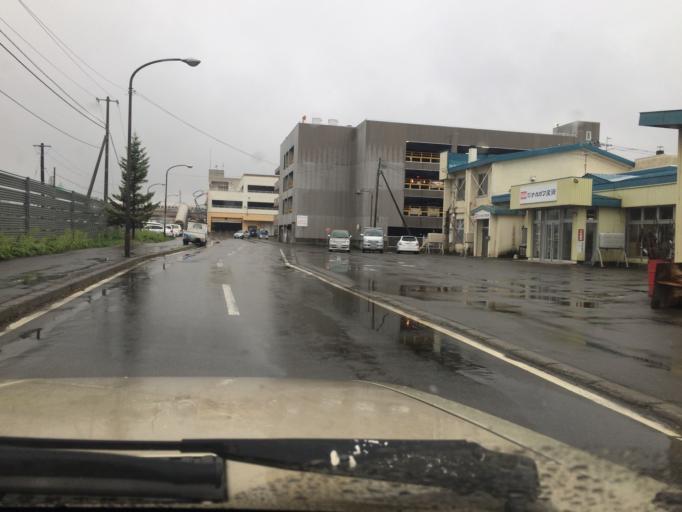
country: JP
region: Hokkaido
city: Obihiro
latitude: 42.9103
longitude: 143.0515
